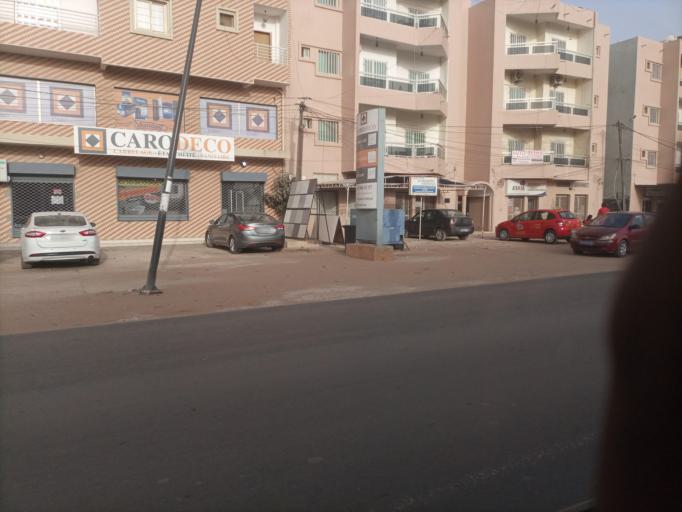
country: SN
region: Thies
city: Warang
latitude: 14.4378
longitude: -16.9778
